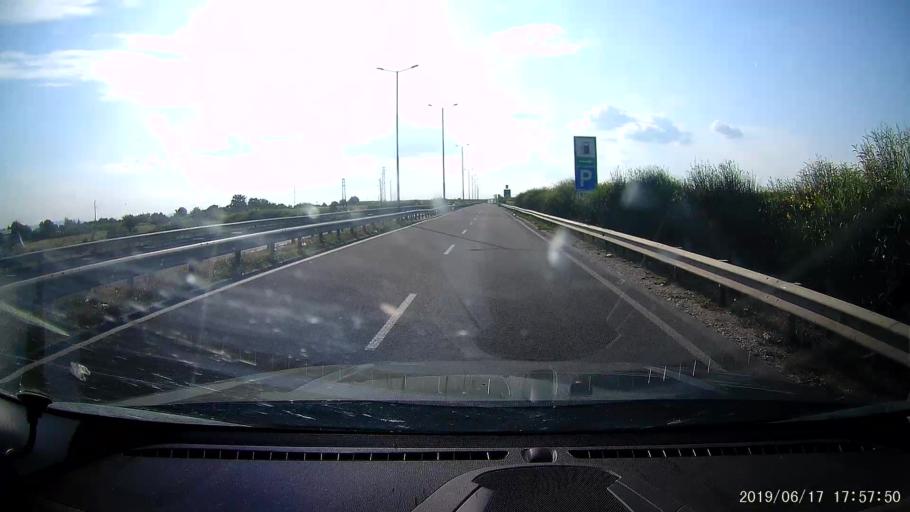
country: BG
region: Khaskovo
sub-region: Obshtina Svilengrad
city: Svilengrad
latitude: 41.7233
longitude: 26.3297
